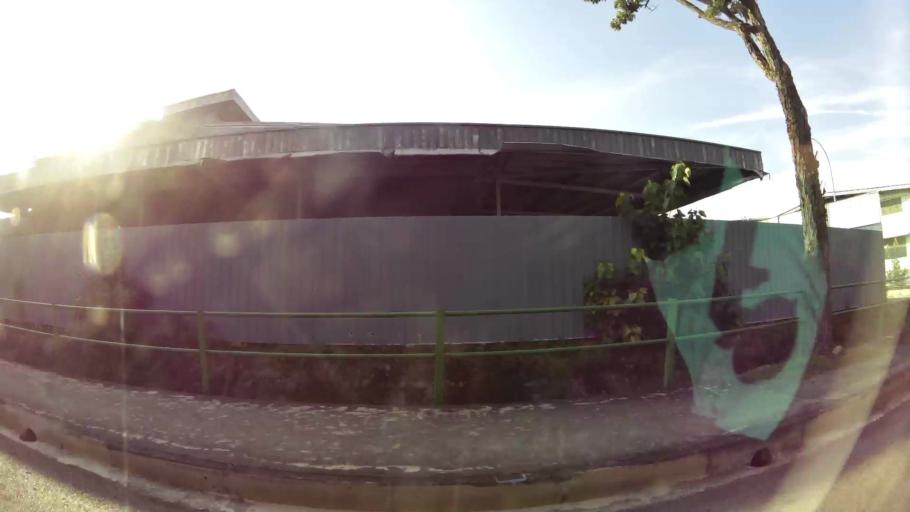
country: SG
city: Singapore
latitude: 1.3228
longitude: 103.8781
